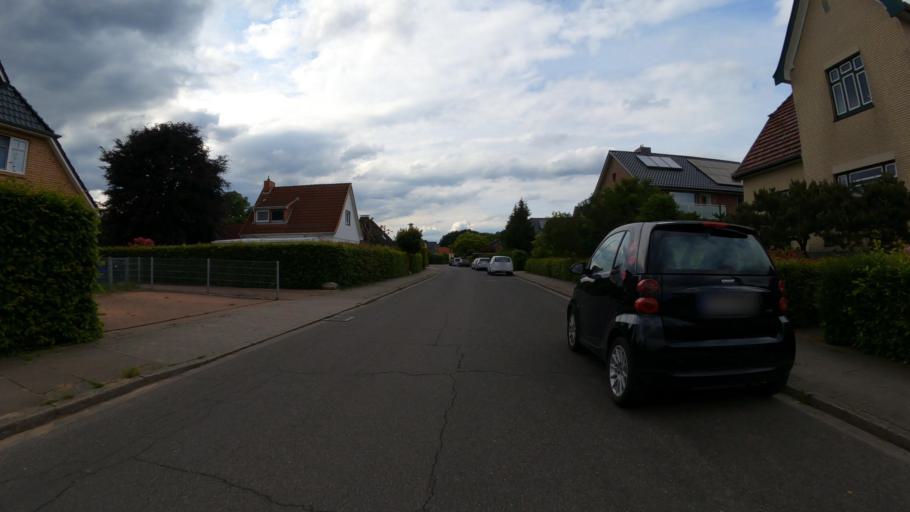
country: DE
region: Schleswig-Holstein
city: Rellingen
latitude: 53.6434
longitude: 9.8191
